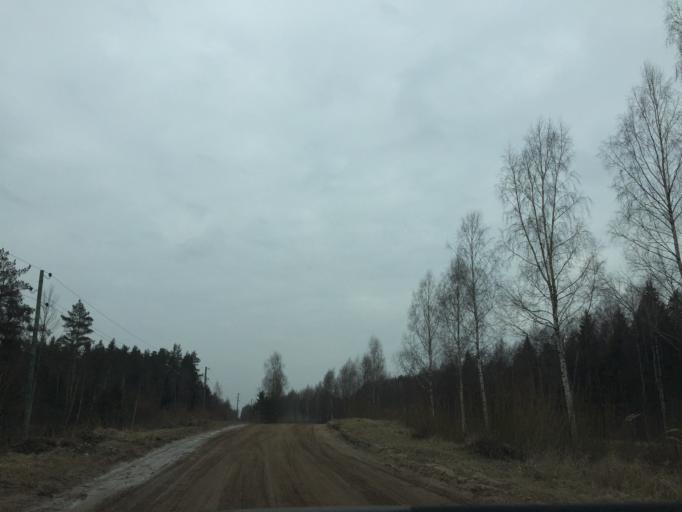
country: LV
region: Kekava
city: Balozi
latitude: 56.7900
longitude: 24.1345
